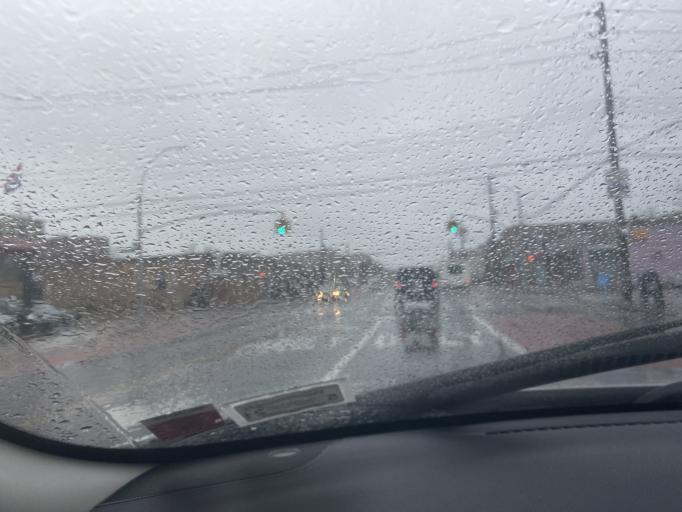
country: US
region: New York
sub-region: Kings County
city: Brooklyn
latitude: 40.6479
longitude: -73.9299
